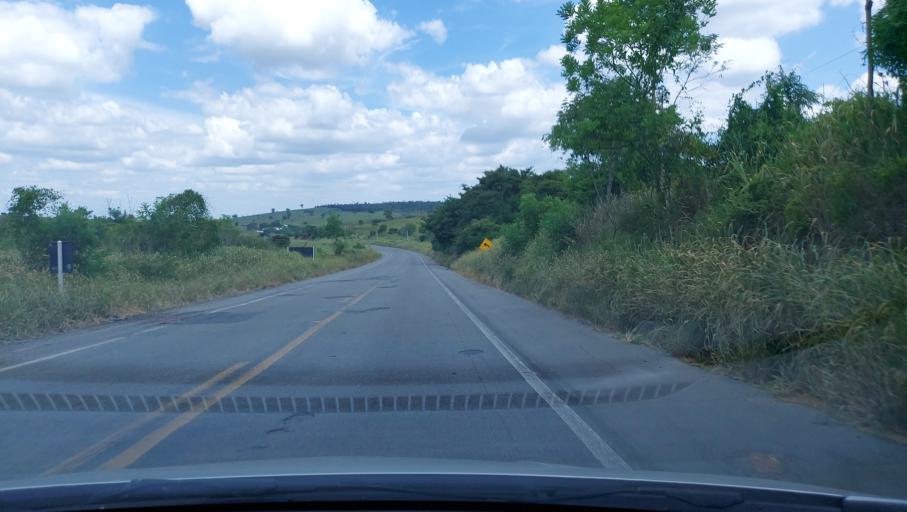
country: BR
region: Bahia
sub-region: Andarai
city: Vera Cruz
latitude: -12.4641
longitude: -40.9078
